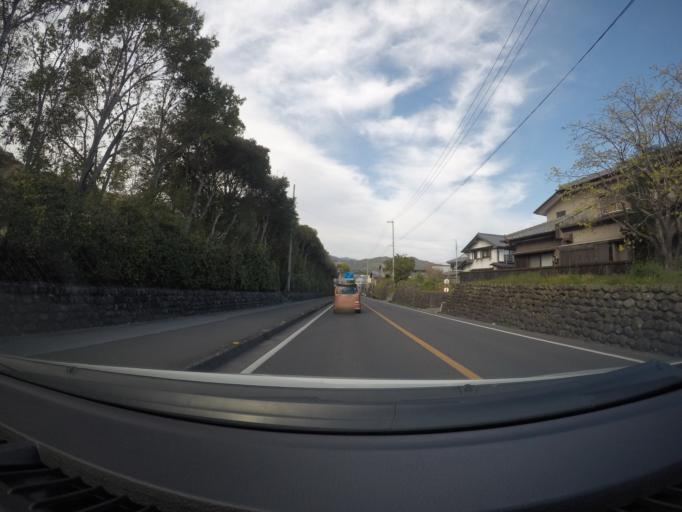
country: JP
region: Kochi
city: Kochi-shi
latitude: 33.6142
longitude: 133.7122
